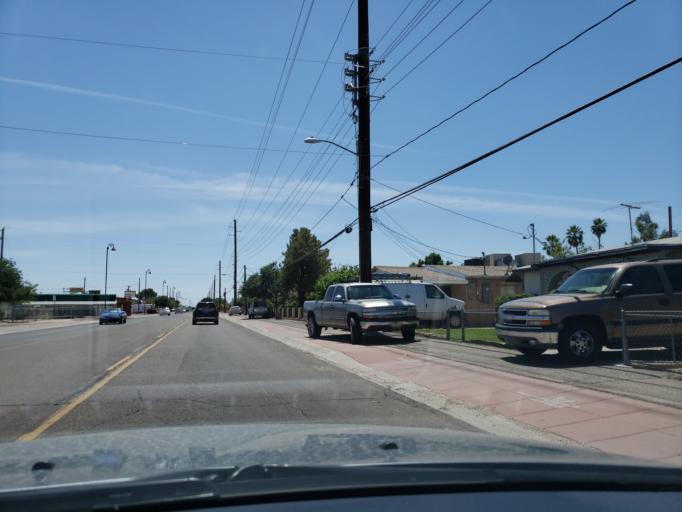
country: US
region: Arizona
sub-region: Maricopa County
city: Guadalupe
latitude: 33.3740
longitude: -111.9632
